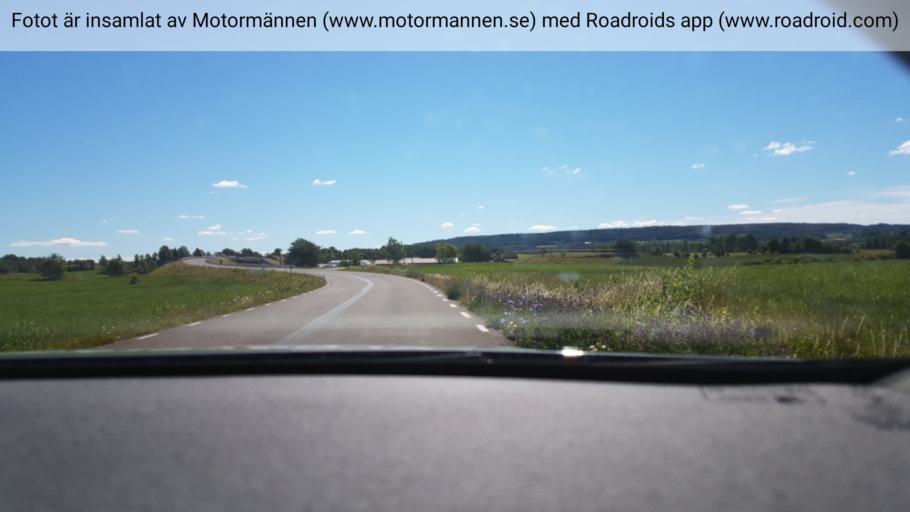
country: SE
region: Vaestra Goetaland
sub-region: Falkopings Kommun
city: Akarp
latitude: 58.2550
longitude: 13.6790
